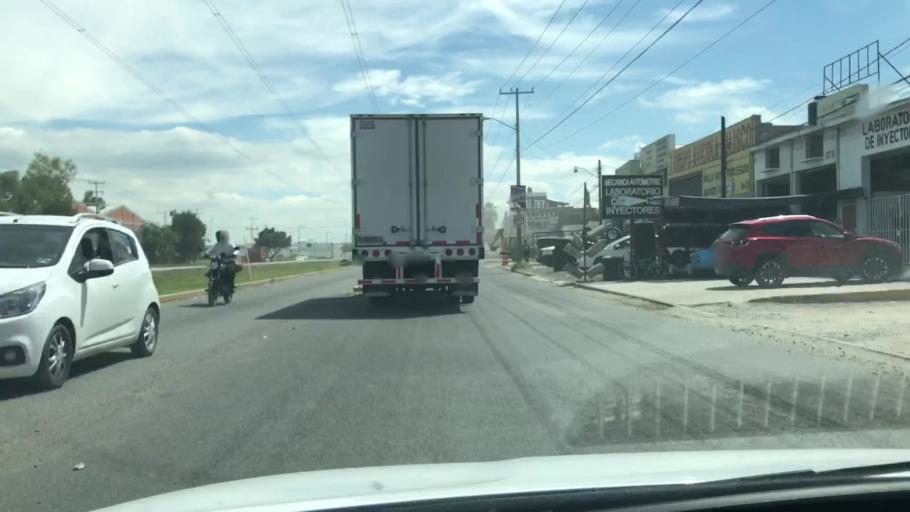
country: MX
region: Guanajuato
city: Celaya
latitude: 20.5512
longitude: -100.8104
